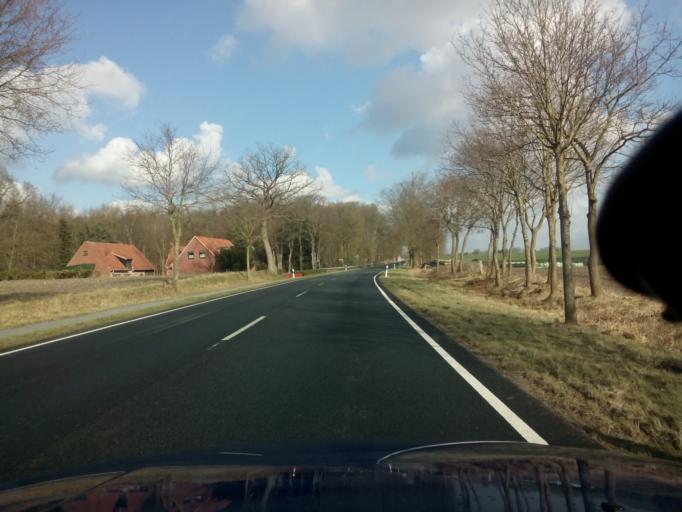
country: DE
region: Lower Saxony
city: Vollersode
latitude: 53.3725
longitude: 8.9475
